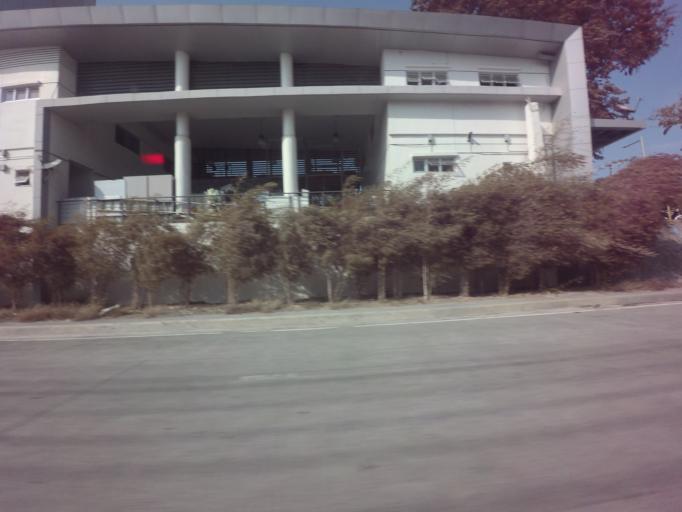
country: PH
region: Calabarzon
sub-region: Province of Rizal
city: Taguig
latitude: 14.5026
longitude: 121.0430
